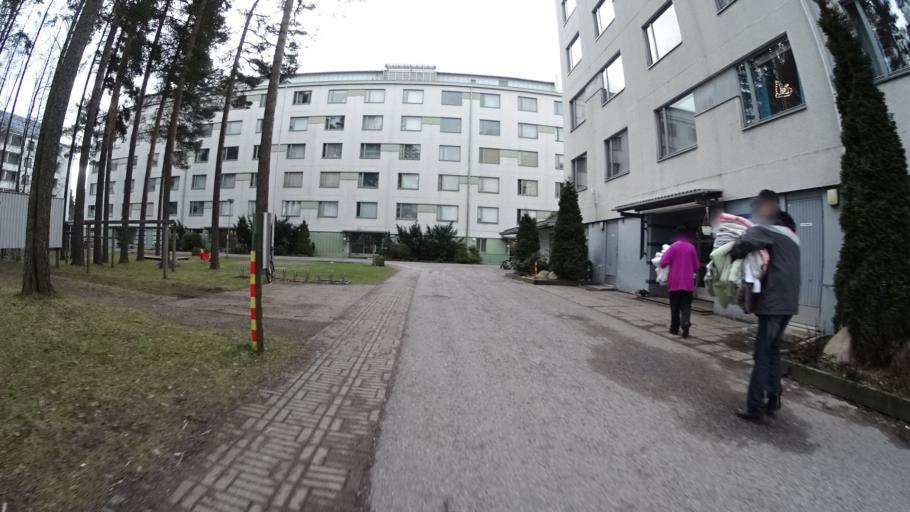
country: FI
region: Uusimaa
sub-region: Helsinki
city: Kilo
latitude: 60.2272
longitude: 24.7601
